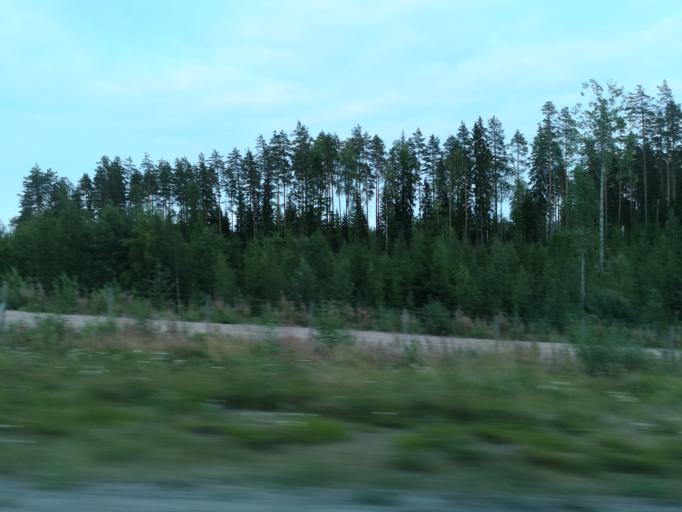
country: FI
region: Central Finland
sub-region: Jyvaeskylae
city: Toivakka
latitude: 62.0128
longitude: 26.0473
